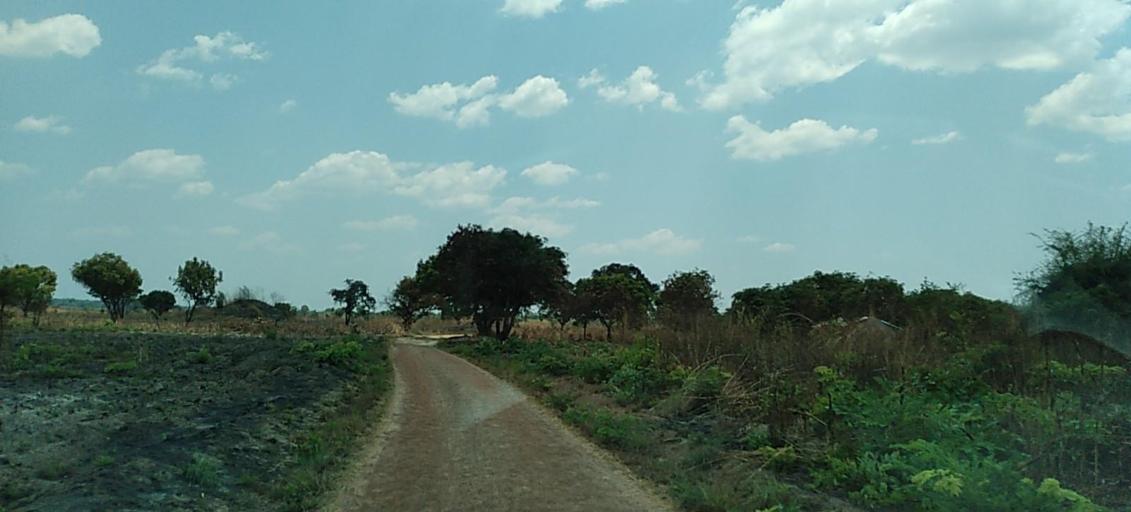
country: ZM
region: Copperbelt
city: Chililabombwe
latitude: -12.4895
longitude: 27.6662
